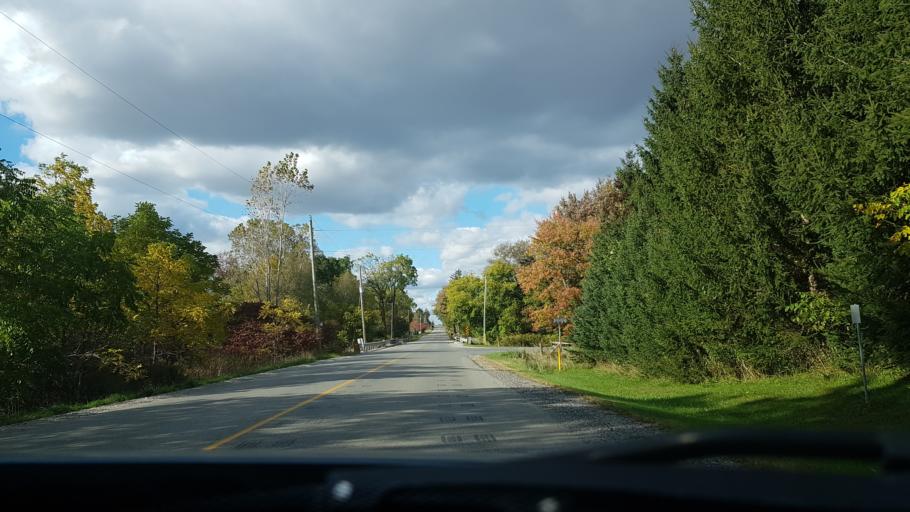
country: CA
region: Ontario
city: Delaware
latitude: 43.0054
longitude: -81.3986
